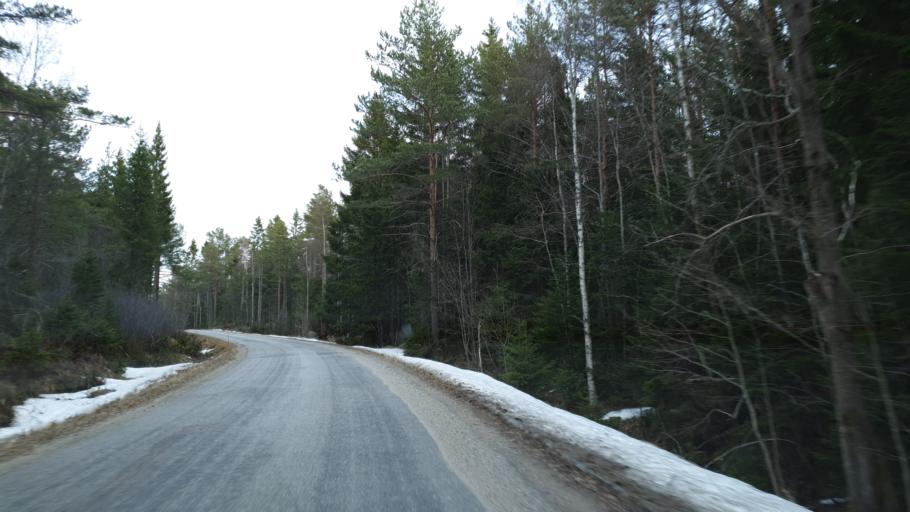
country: SE
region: Vaesternorrland
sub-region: Sundsvalls Kommun
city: Njurundabommen
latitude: 61.9631
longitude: 17.3698
